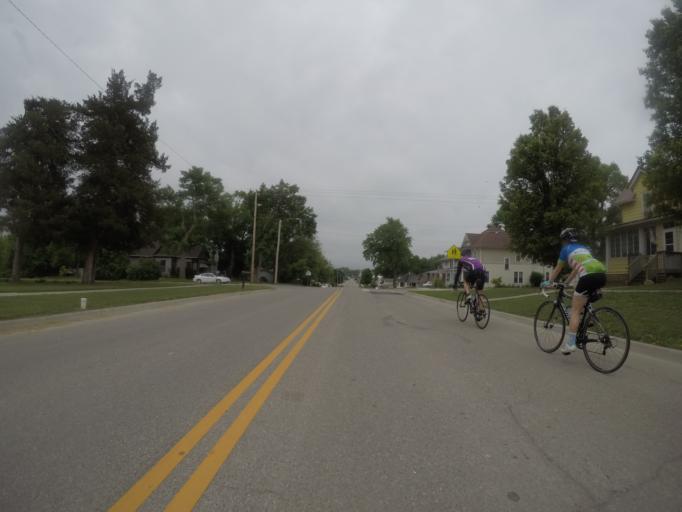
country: US
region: Kansas
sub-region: Pottawatomie County
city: Westmoreland
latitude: 39.4937
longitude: -96.1699
